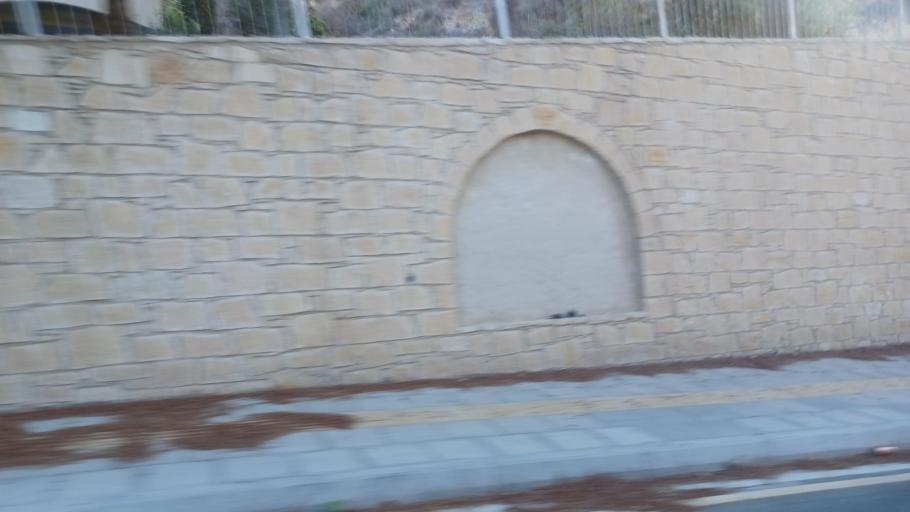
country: CY
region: Pafos
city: Mesogi
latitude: 34.7924
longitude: 32.4844
